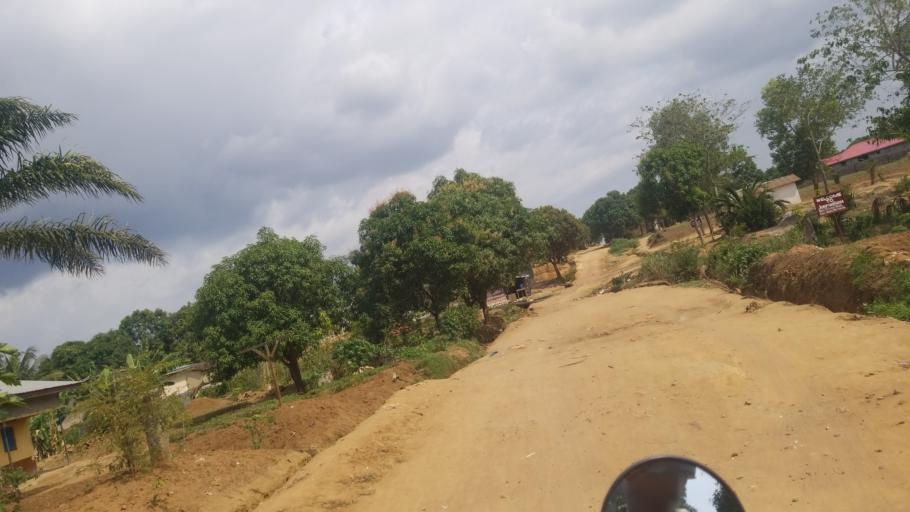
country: SL
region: Western Area
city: Waterloo
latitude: 8.3439
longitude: -13.0528
